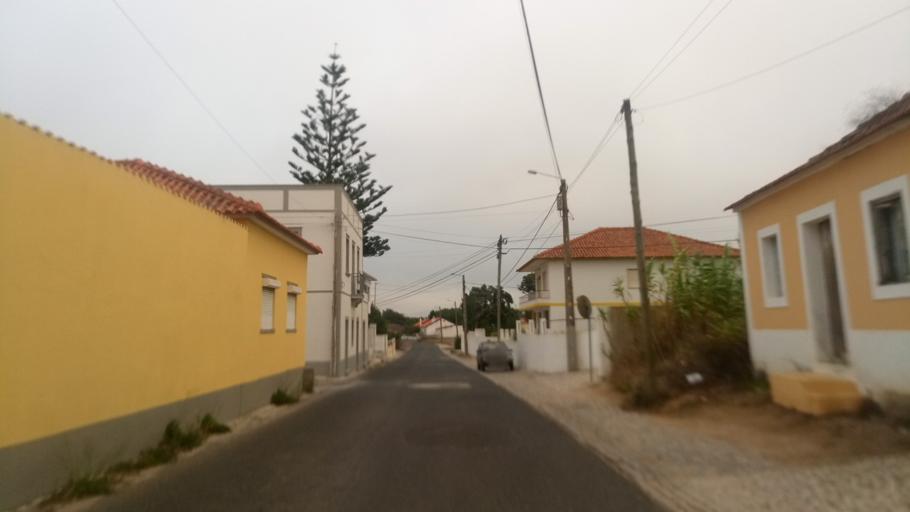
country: PT
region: Leiria
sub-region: Caldas da Rainha
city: Caldas da Rainha
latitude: 39.4508
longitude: -9.1774
